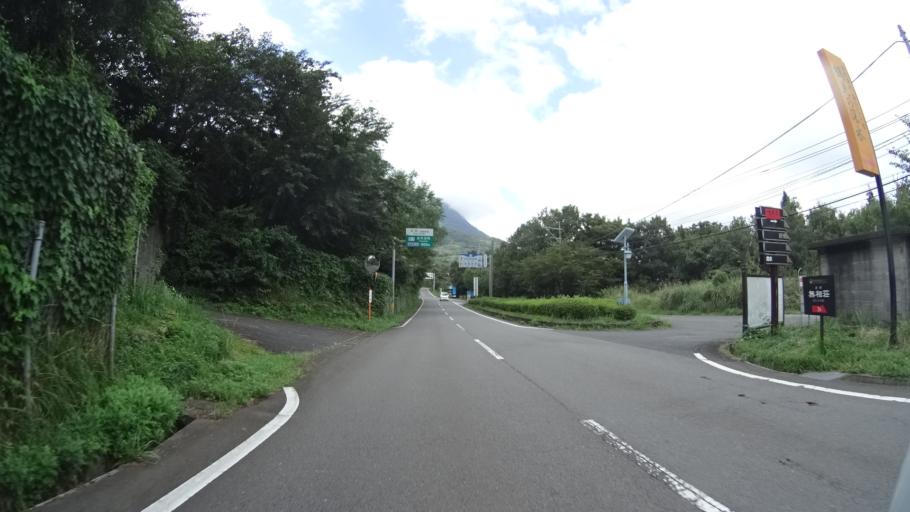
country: JP
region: Oita
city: Beppu
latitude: 33.3065
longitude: 131.4041
